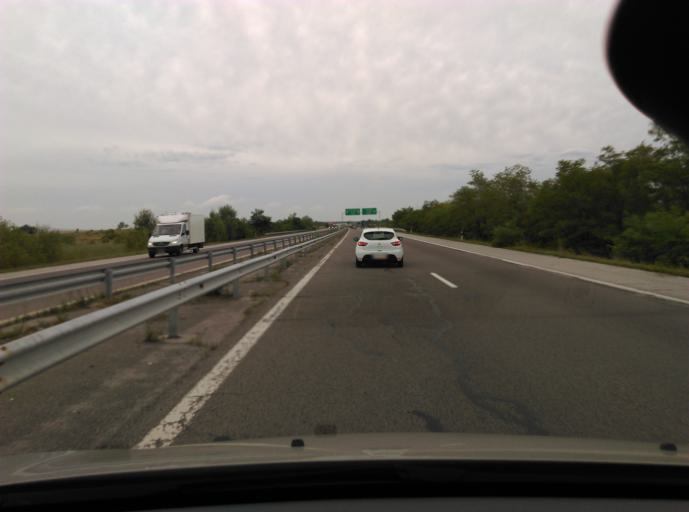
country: BG
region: Stara Zagora
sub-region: Obshtina Chirpan
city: Chirpan
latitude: 42.1930
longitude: 25.2244
